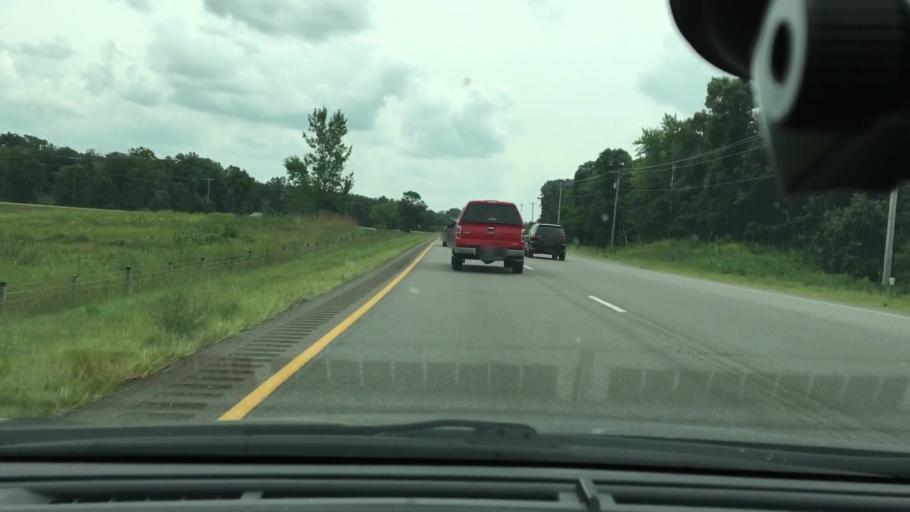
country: US
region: Minnesota
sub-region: Sherburne County
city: Elk River
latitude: 45.3554
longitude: -93.5615
